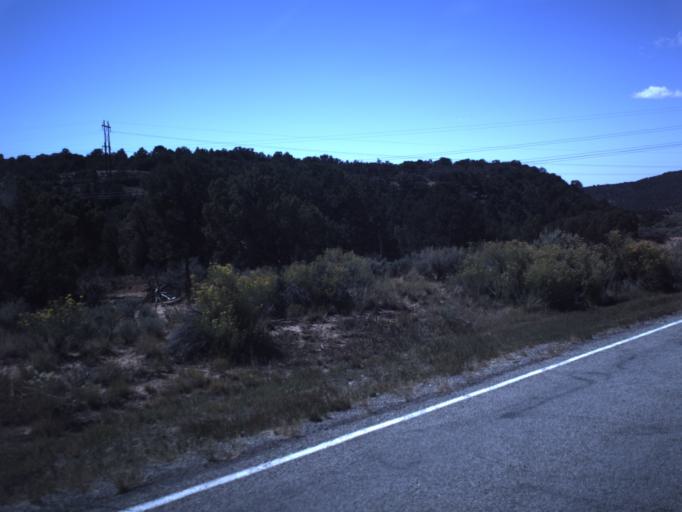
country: US
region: Utah
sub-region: Grand County
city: Moab
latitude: 38.3192
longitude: -109.3300
